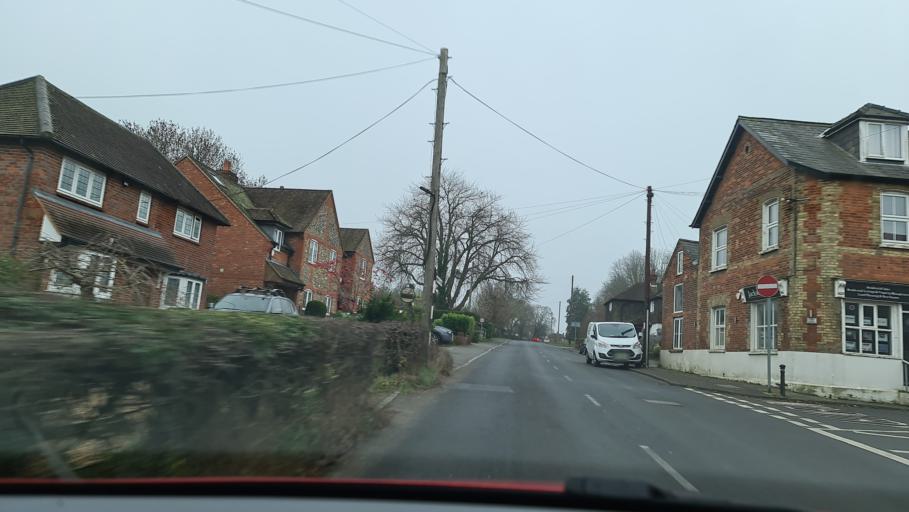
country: GB
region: England
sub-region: Buckinghamshire
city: Beaconsfield
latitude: 51.6374
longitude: -0.6916
